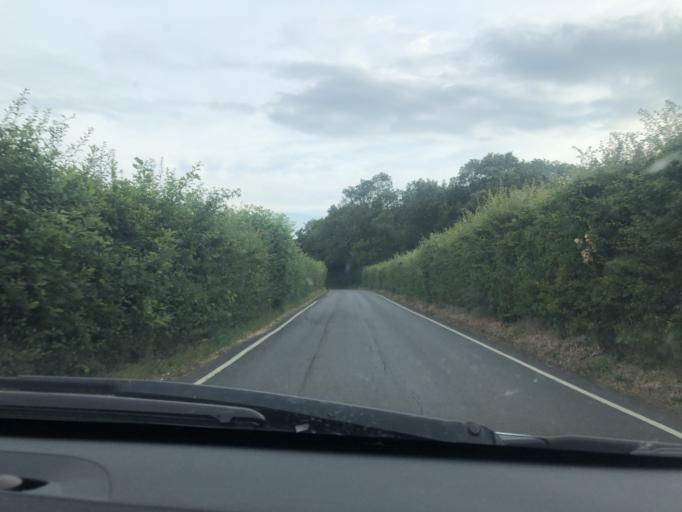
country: GB
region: England
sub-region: Kent
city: Sturry
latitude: 51.3273
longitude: 1.1476
